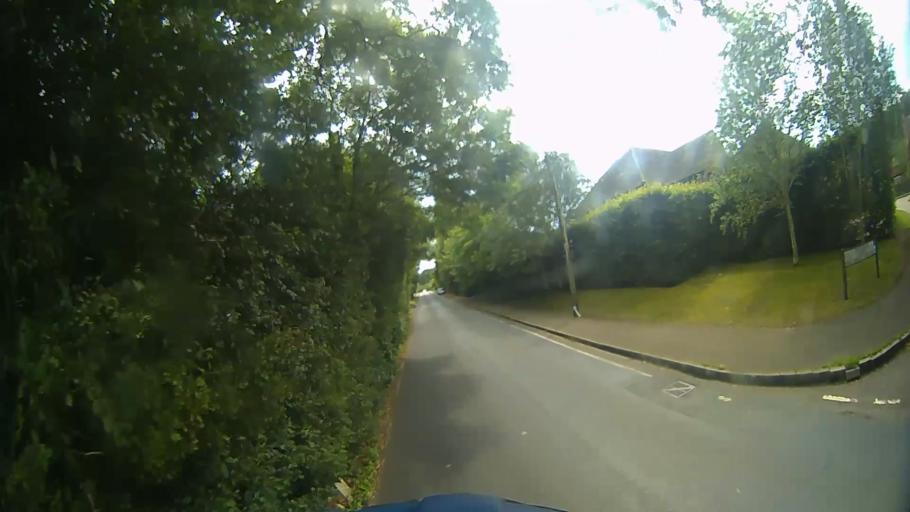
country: GB
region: England
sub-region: Hampshire
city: Kingsley
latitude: 51.1565
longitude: -0.8515
